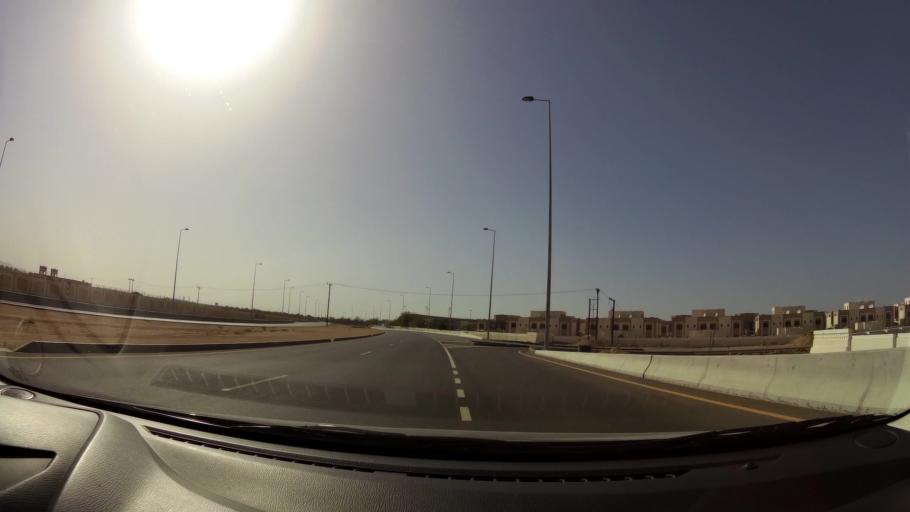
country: OM
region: Muhafazat Masqat
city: Bawshar
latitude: 23.5780
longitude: 58.2760
